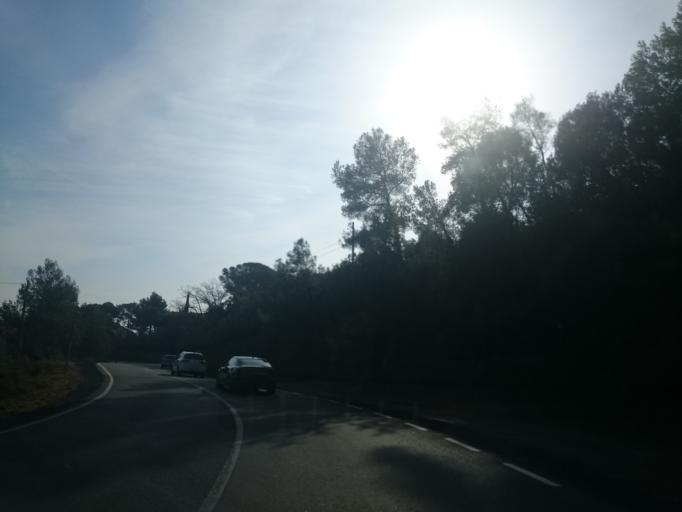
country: ES
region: Catalonia
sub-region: Provincia de Barcelona
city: Begues
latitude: 41.3152
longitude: 1.9598
